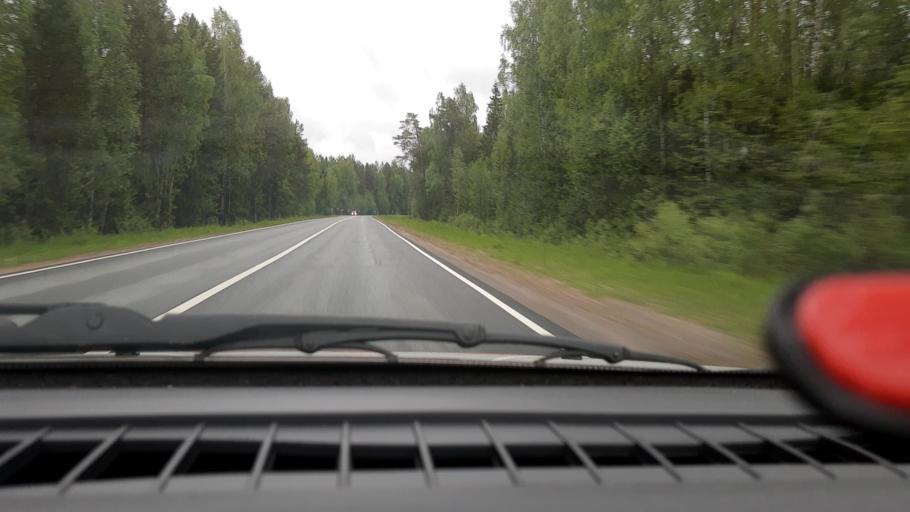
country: RU
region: Nizjnij Novgorod
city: Krasnyye Baki
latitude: 57.2228
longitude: 45.4870
